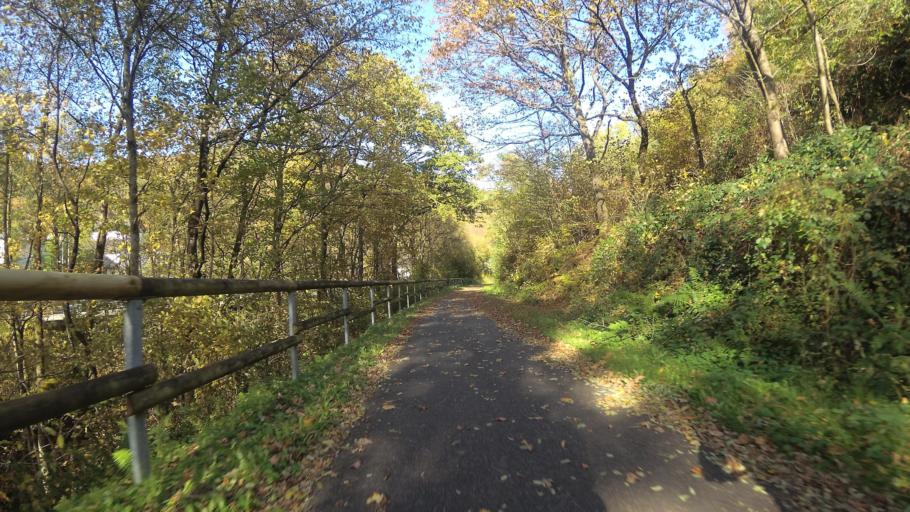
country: DE
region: Rheinland-Pfalz
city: Gutweiler
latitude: 49.7062
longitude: 6.7320
